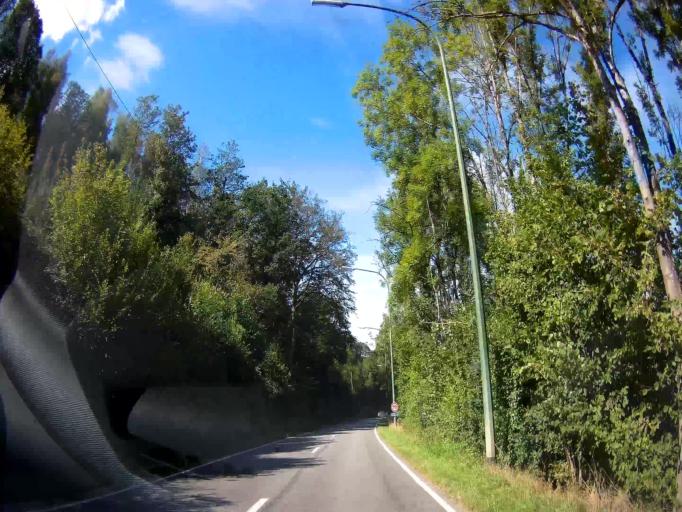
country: BE
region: Wallonia
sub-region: Province du Luxembourg
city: La Roche-en-Ardenne
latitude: 50.1864
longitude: 5.5441
